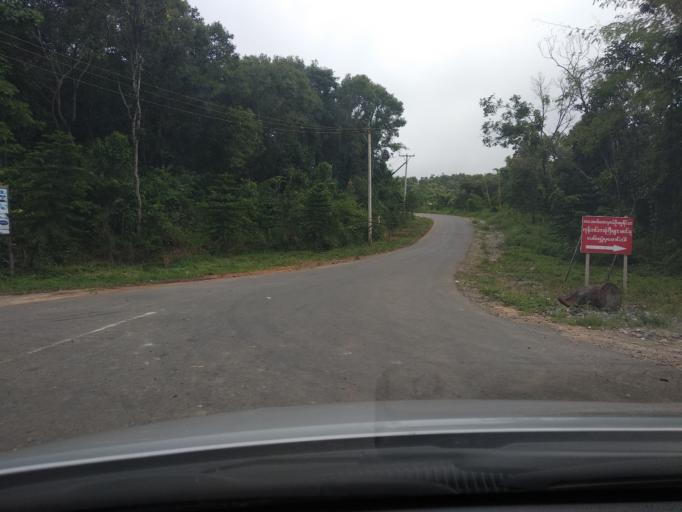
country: MM
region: Mandalay
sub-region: Pyin Oo Lwin District
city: Pyin Oo Lwin
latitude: 21.9233
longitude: 96.3751
